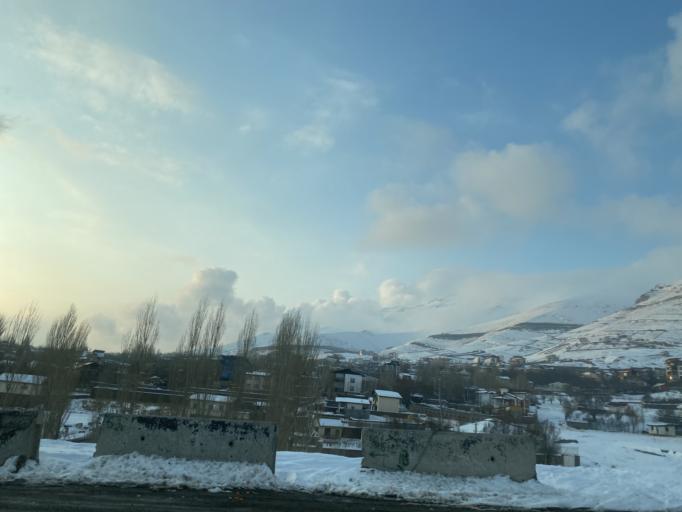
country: IR
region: Tehran
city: Damavand
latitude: 35.7675
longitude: 52.0269
